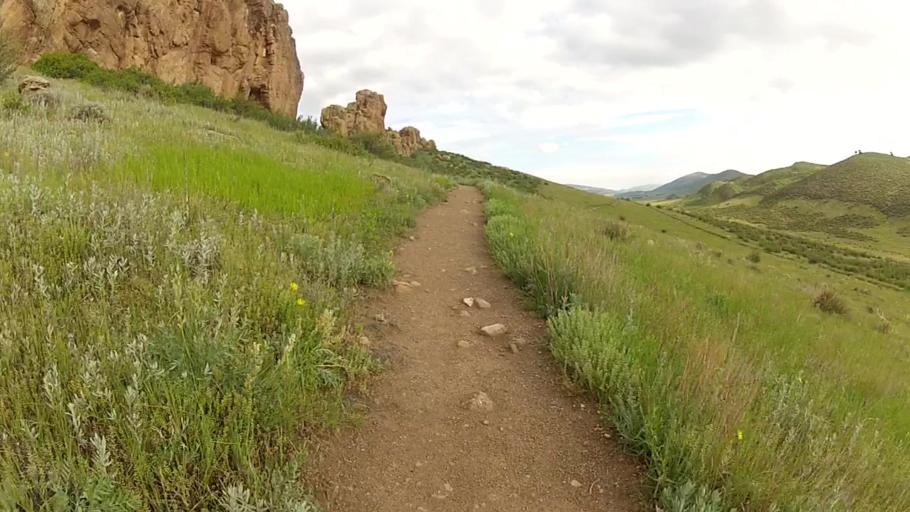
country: US
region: Colorado
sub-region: Larimer County
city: Loveland
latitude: 40.4229
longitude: -105.1616
